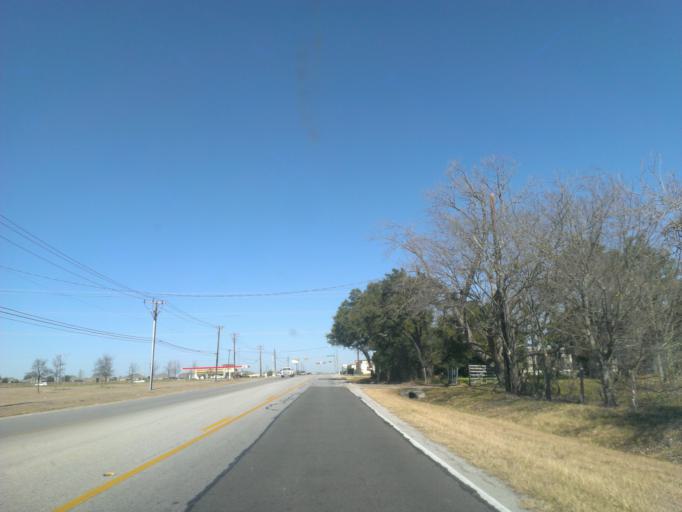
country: US
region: Texas
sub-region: Williamson County
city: Hutto
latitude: 30.5444
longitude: -97.6143
